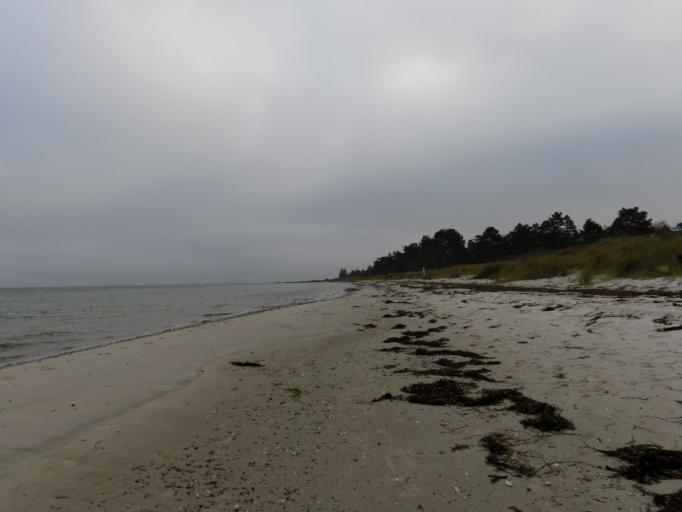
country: DK
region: Central Jutland
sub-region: Arhus Kommune
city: Malling
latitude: 55.9719
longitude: 10.2564
